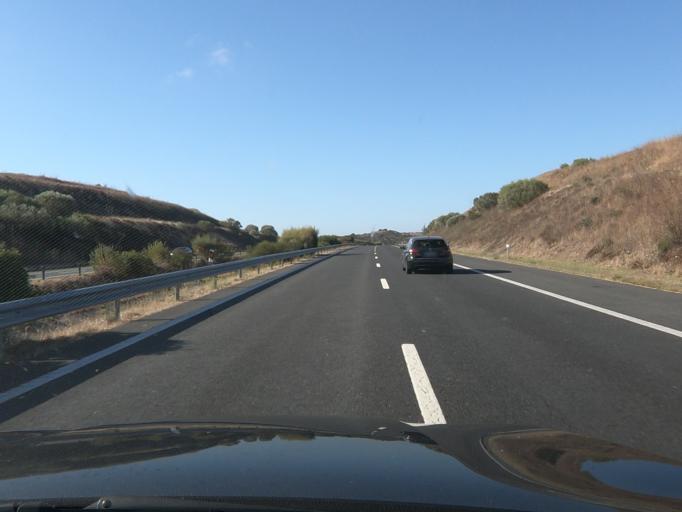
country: PT
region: Beja
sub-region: Aljustrel
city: Aljustrel
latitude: 37.8539
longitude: -8.2293
